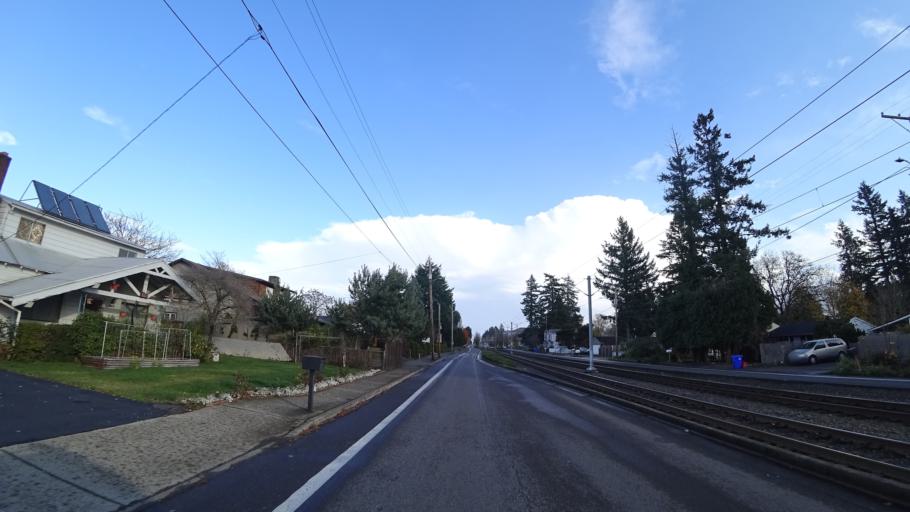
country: US
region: Oregon
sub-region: Multnomah County
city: Lents
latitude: 45.5226
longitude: -122.5424
